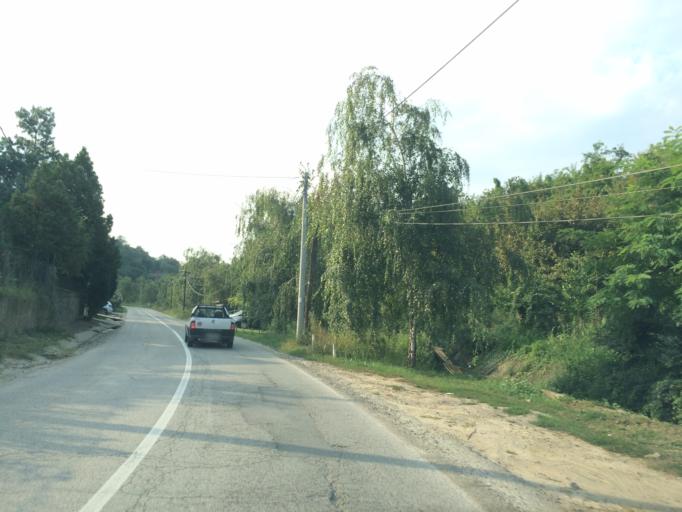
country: RS
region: Autonomna Pokrajina Vojvodina
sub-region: Juznobacki Okrug
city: Novi Sad
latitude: 45.2148
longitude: 19.8066
